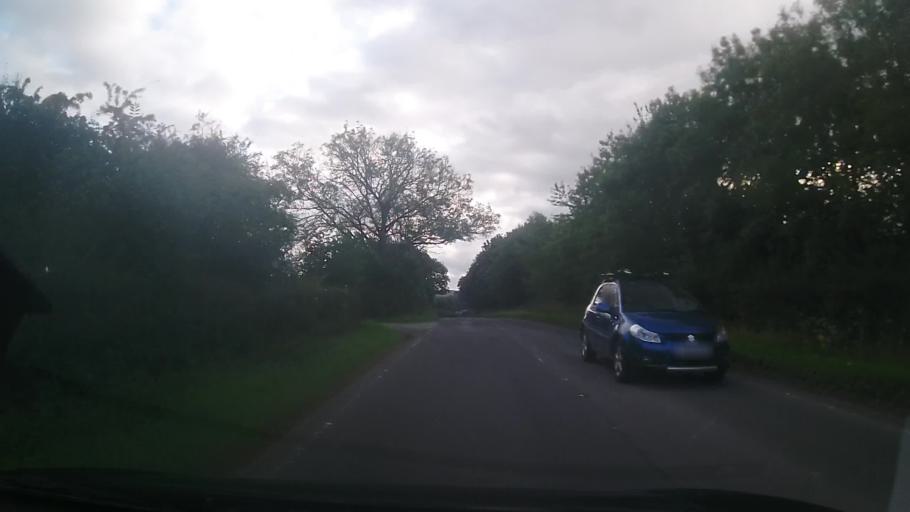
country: GB
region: England
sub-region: Shropshire
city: Bishop's Castle
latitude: 52.4927
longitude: -2.9894
